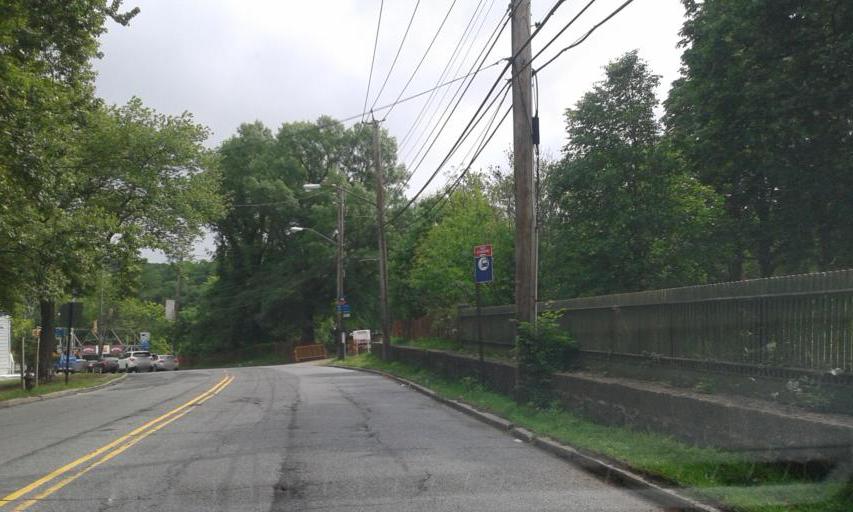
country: US
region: New York
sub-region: Richmond County
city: Staten Island
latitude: 40.5710
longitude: -74.1477
